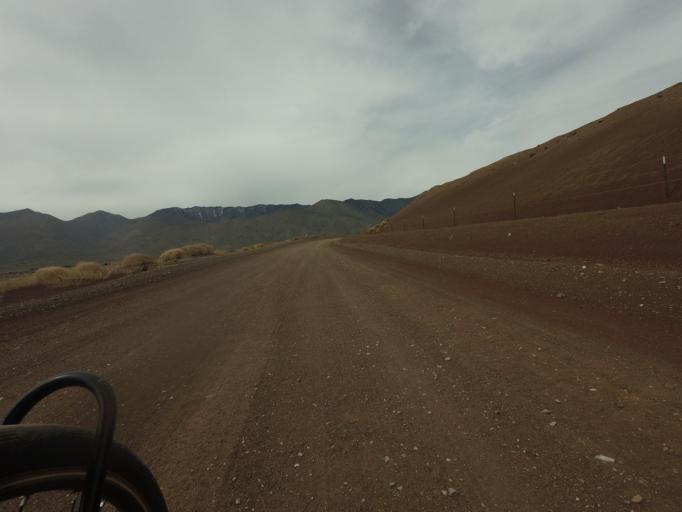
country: US
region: California
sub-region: Kern County
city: Inyokern
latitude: 35.9775
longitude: -117.9144
